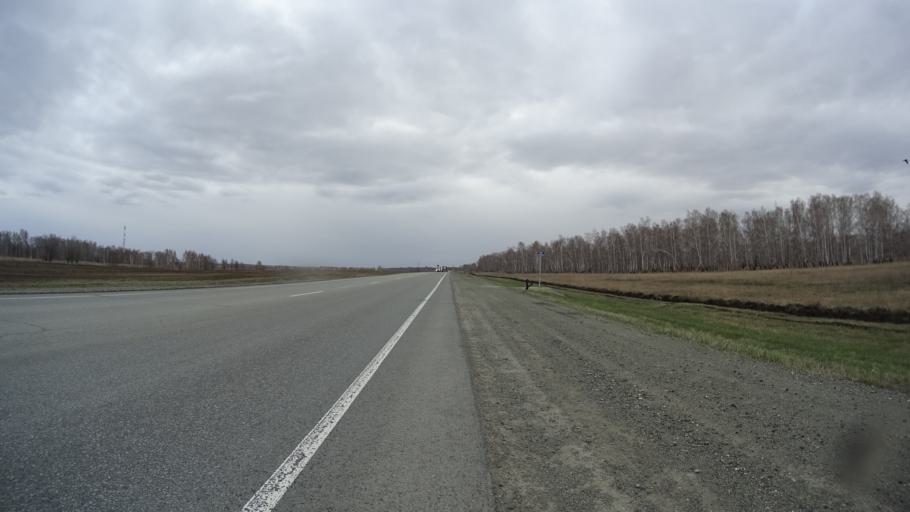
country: RU
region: Chelyabinsk
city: Krasnogorskiy
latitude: 54.6900
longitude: 61.2486
